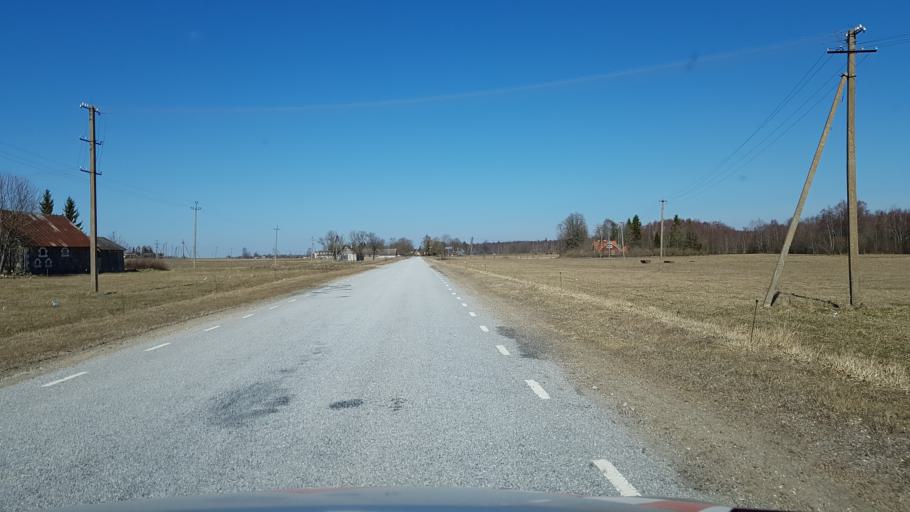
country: EE
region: Jaervamaa
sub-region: Koeru vald
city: Koeru
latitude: 59.0448
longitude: 26.0903
